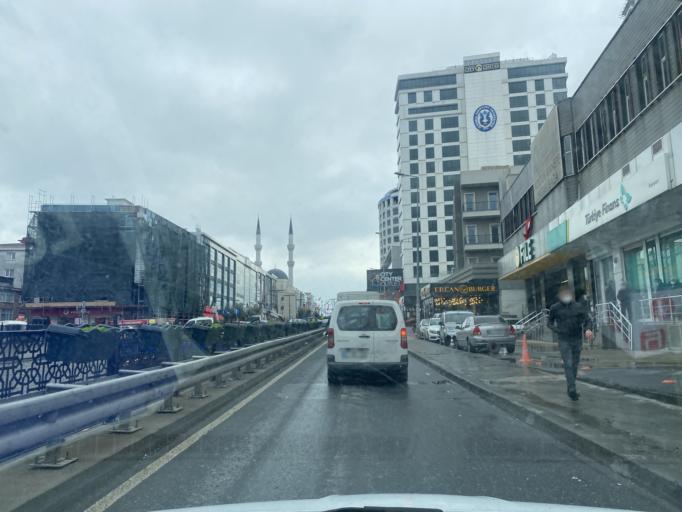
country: TR
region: Istanbul
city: Esenyurt
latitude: 41.0217
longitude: 28.6870
